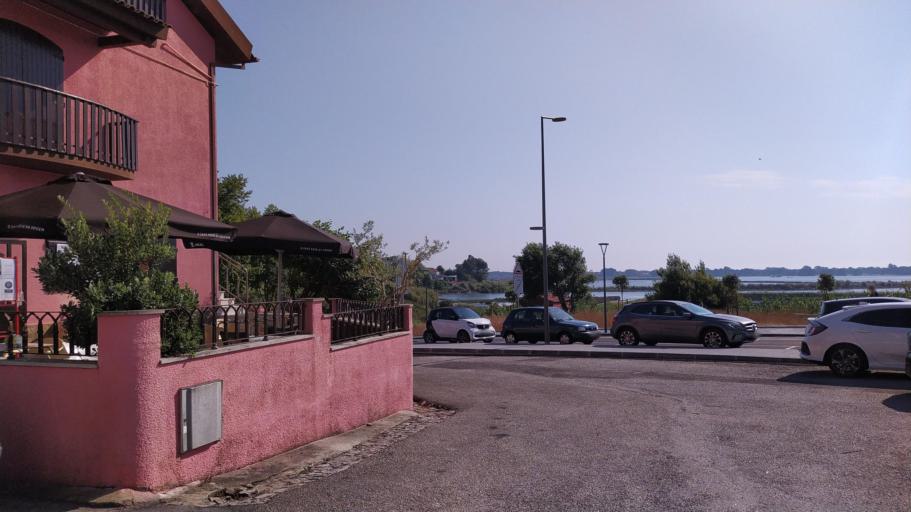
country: PT
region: Aveiro
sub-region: Aveiro
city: Aradas
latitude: 40.6296
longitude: -8.6595
